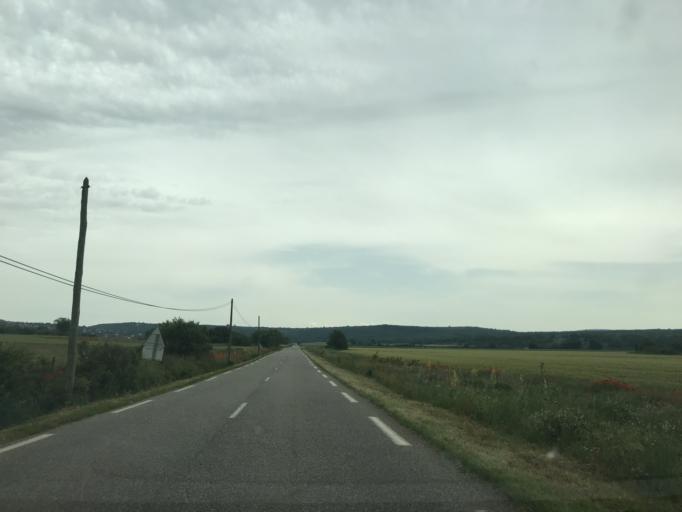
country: FR
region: Provence-Alpes-Cote d'Azur
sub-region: Departement du Var
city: Ginasservis
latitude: 43.6443
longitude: 5.8302
